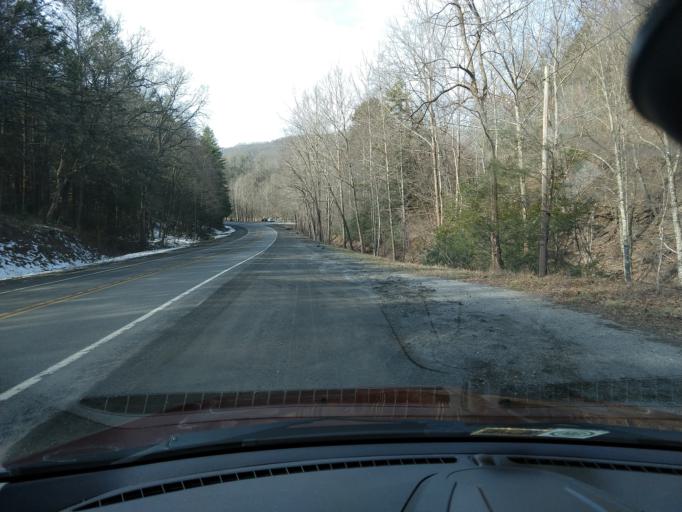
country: US
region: West Virginia
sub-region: Pocahontas County
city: Marlinton
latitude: 38.1991
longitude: -80.1324
